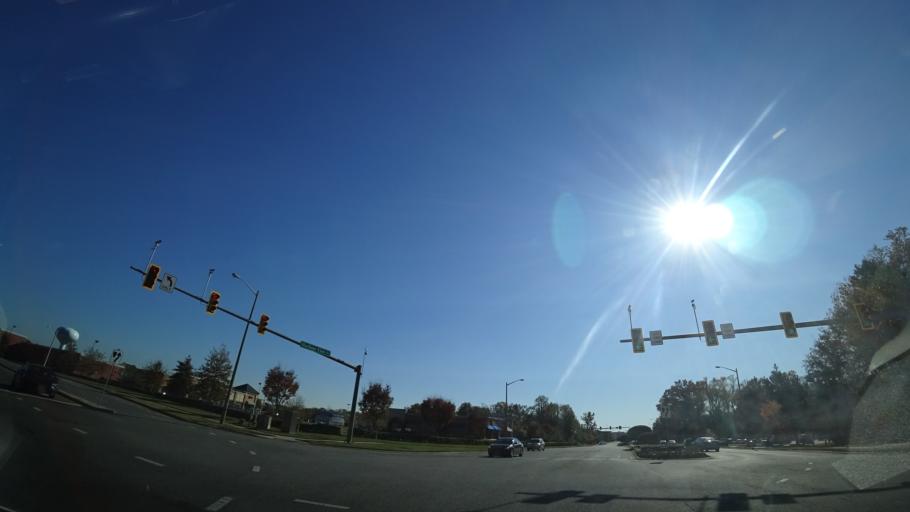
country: US
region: Virginia
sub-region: City of Portsmouth
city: Portsmouth Heights
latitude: 36.8766
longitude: -76.4382
